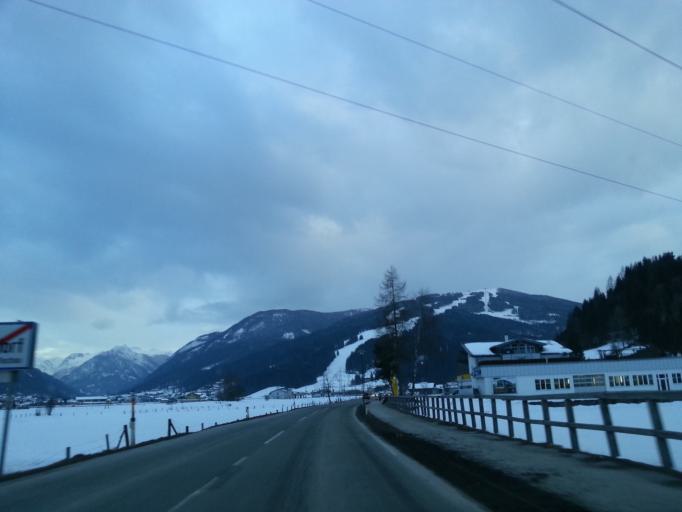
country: AT
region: Salzburg
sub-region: Politischer Bezirk Sankt Johann im Pongau
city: Flachau
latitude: 47.3696
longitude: 13.3869
